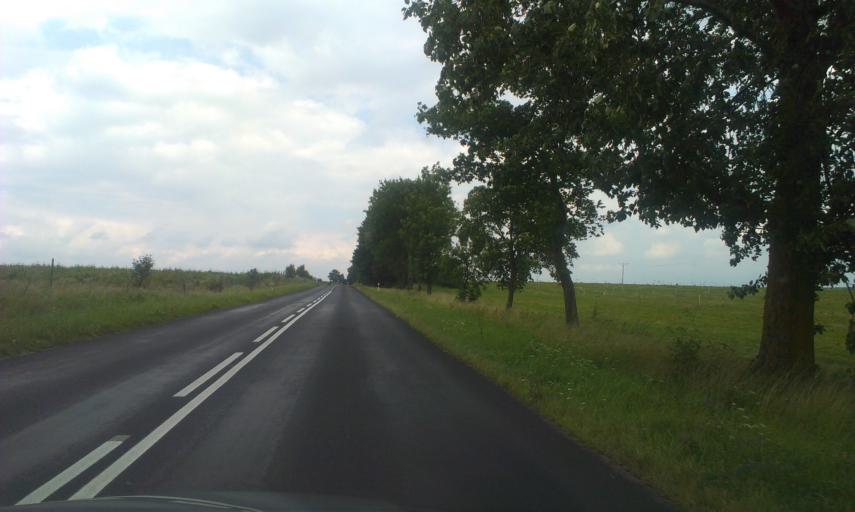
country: PL
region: West Pomeranian Voivodeship
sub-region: Powiat swidwinski
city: Polczyn-Zdroj
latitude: 53.8752
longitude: 16.0693
